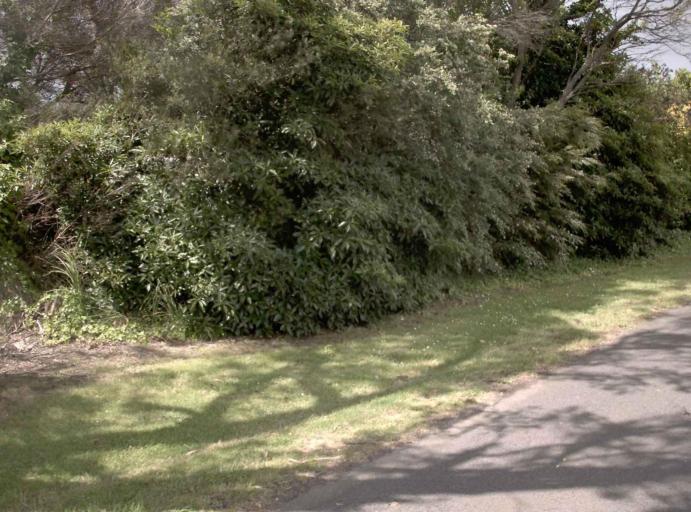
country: AU
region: Victoria
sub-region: Latrobe
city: Moe
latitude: -38.1836
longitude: 146.2393
